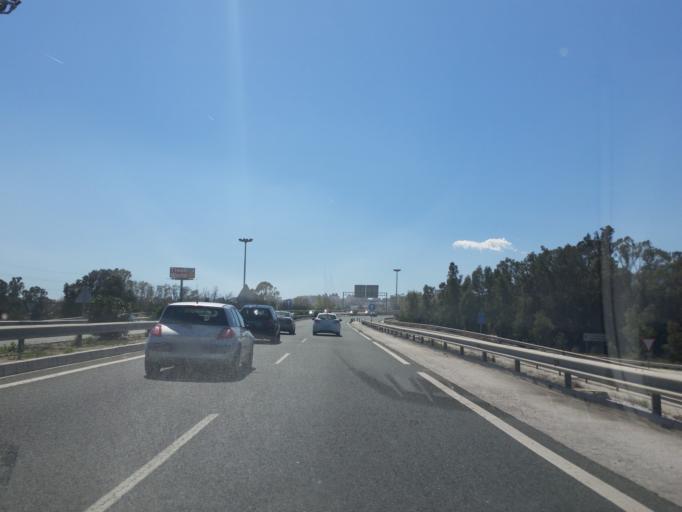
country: ES
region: Andalusia
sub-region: Provincia de Malaga
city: Torremolinos
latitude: 36.6517
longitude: -4.4800
